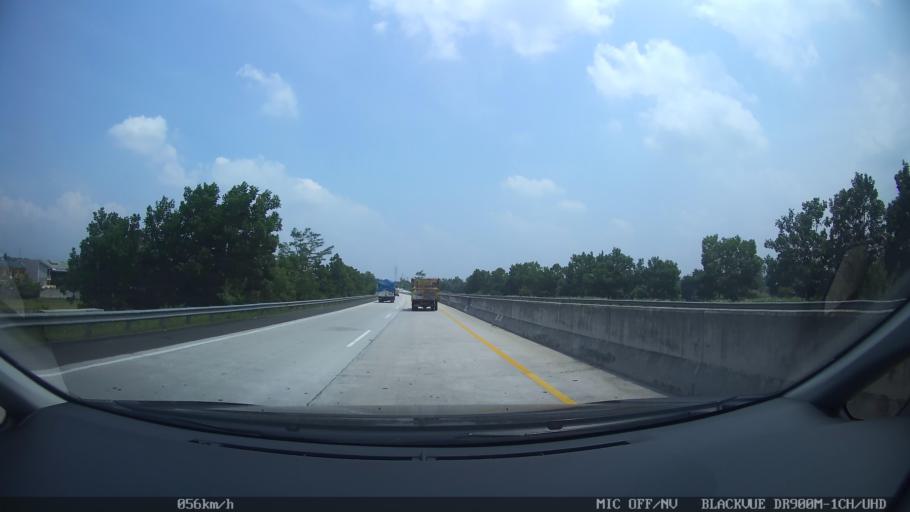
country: ID
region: Lampung
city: Kedaton
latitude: -5.3519
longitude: 105.3225
